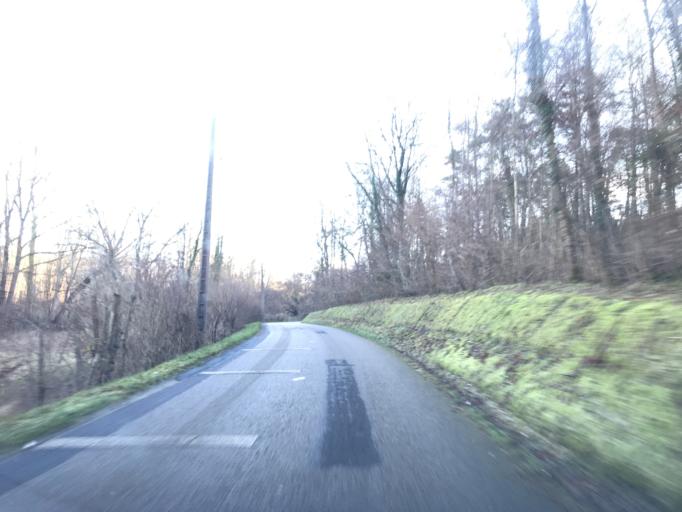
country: FR
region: Haute-Normandie
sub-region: Departement de l'Eure
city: Heudreville-sur-Eure
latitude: 49.0914
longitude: 1.2607
